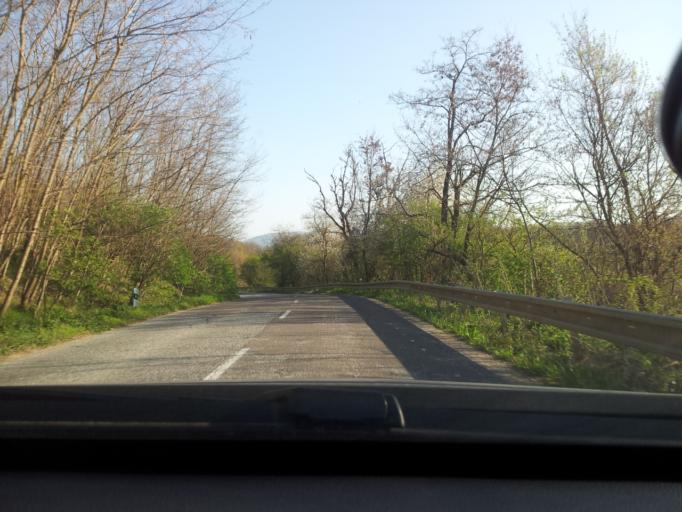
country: SK
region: Nitriansky
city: Tlmace
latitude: 48.2949
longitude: 18.4503
